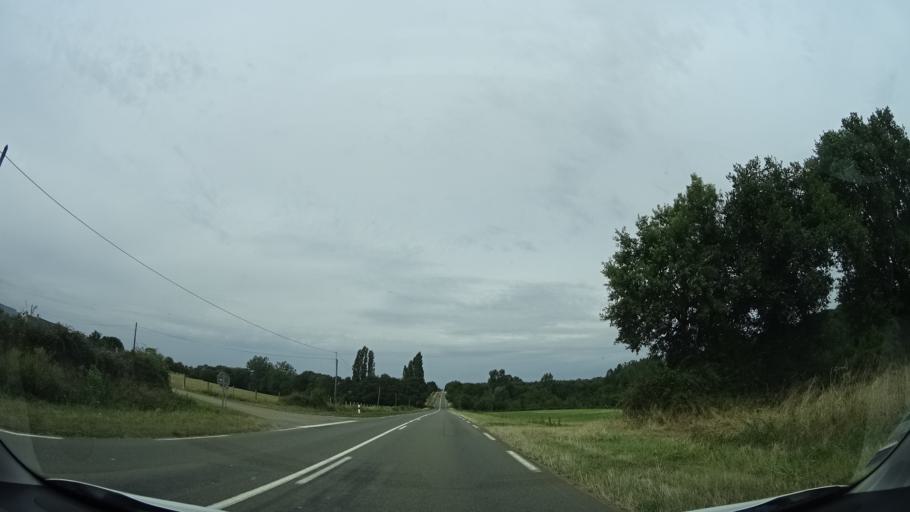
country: FR
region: Pays de la Loire
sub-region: Departement de la Mayenne
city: Meslay-du-Maine
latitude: 47.9199
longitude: -0.4754
